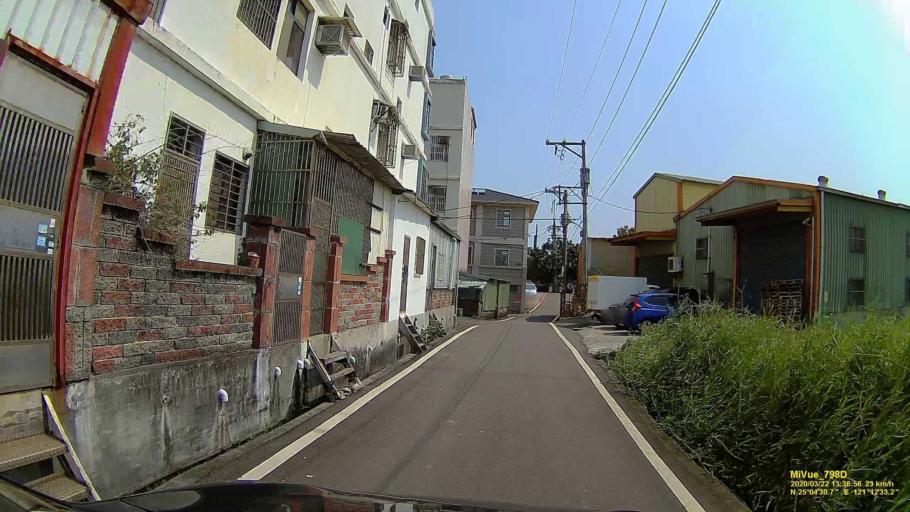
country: TW
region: Taiwan
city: Taoyuan City
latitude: 25.0751
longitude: 121.2093
